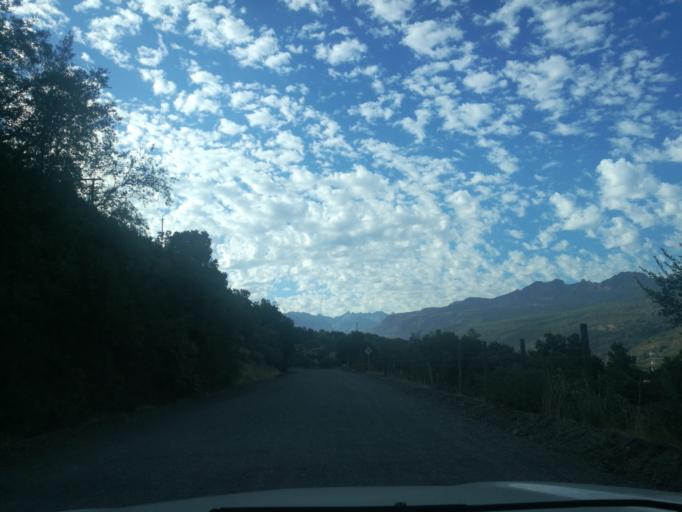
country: CL
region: O'Higgins
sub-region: Provincia de Cachapoal
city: Machali
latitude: -34.2478
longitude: -70.4676
